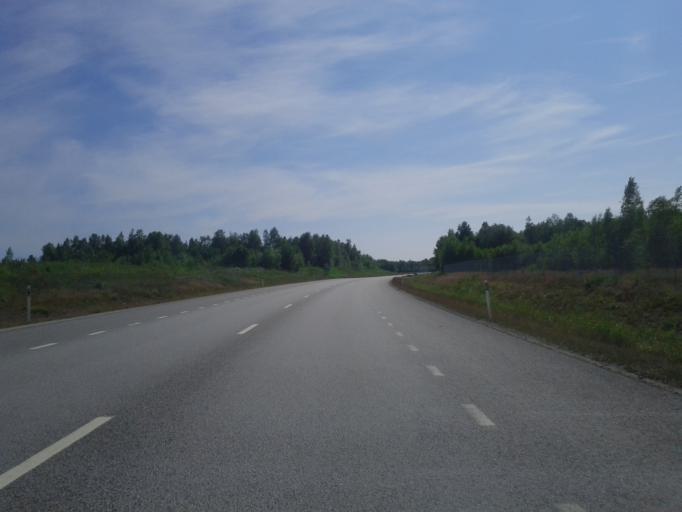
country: SE
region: Vaesterbotten
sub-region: Umea Kommun
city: Umea
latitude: 63.7805
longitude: 20.3033
